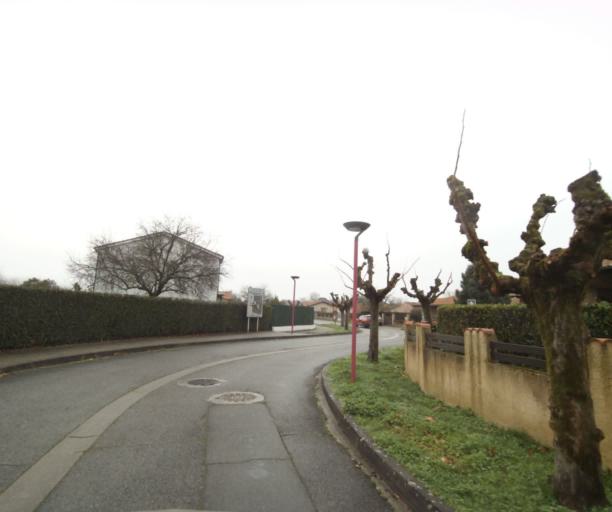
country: FR
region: Midi-Pyrenees
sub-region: Departement de la Haute-Garonne
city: Villemur-sur-Tarn
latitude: 43.8577
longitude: 1.5033
